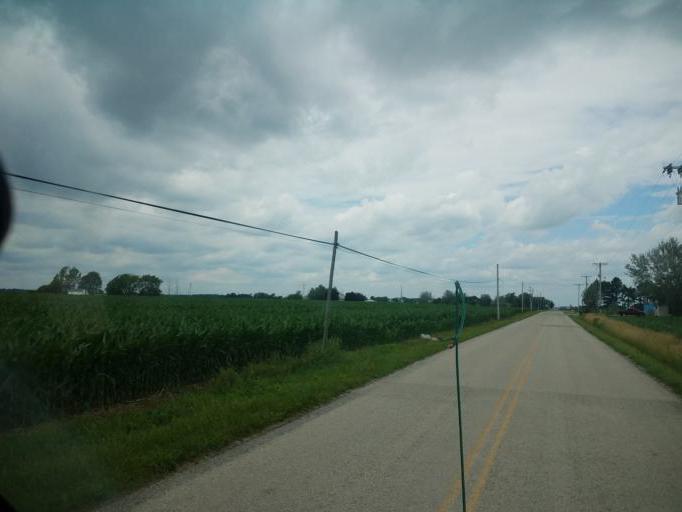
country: US
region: Ohio
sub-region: Richland County
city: Shelby
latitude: 40.8695
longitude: -82.7199
